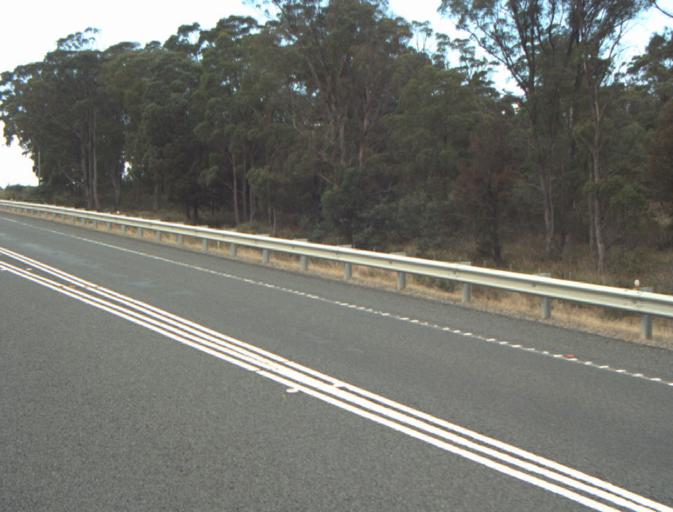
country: AU
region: Tasmania
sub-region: Launceston
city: Mayfield
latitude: -41.2645
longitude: 147.0318
